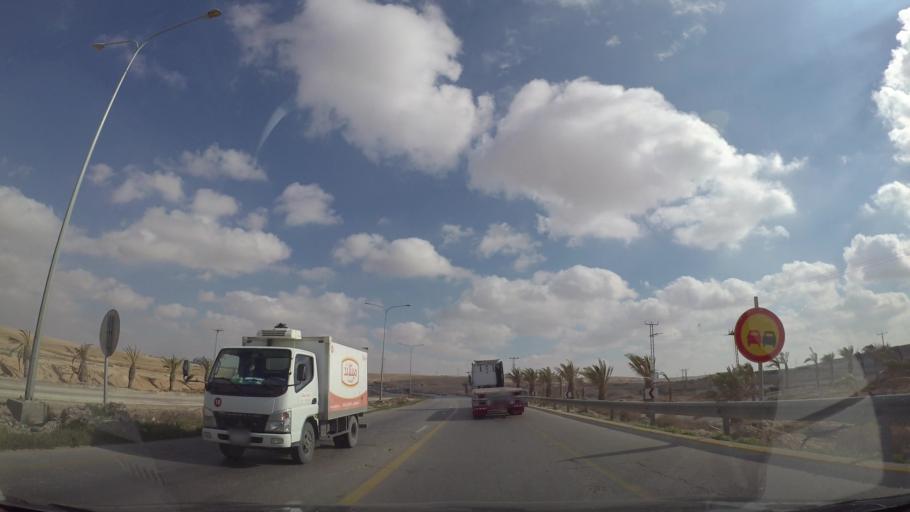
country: JO
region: Amman
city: Al Jizah
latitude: 31.6314
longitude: 35.9853
